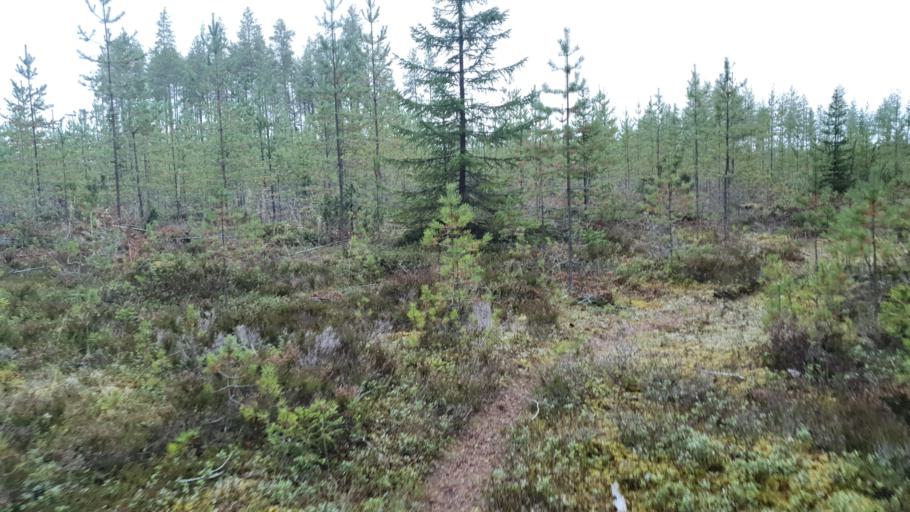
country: FI
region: Kainuu
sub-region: Kehys-Kainuu
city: Kuhmo
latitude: 64.1325
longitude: 29.3898
